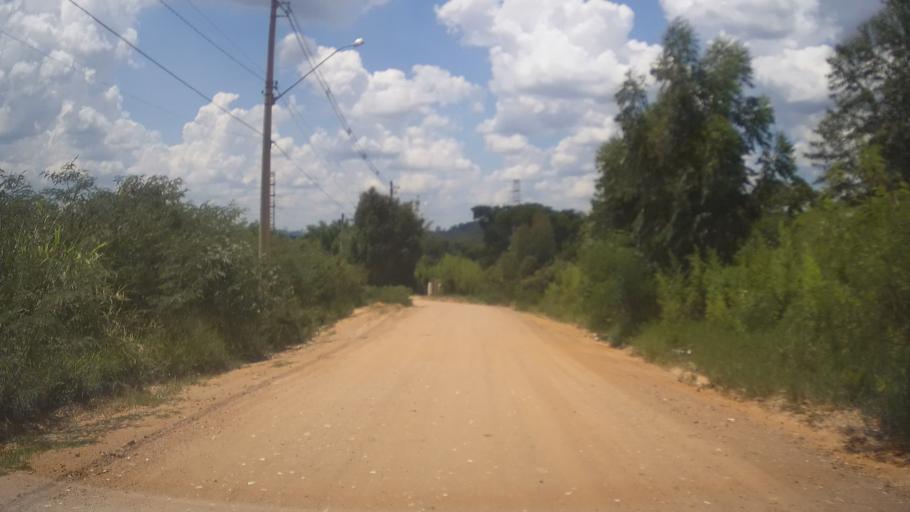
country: BR
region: Sao Paulo
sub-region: Jundiai
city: Jundiai
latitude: -23.1580
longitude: -46.8919
